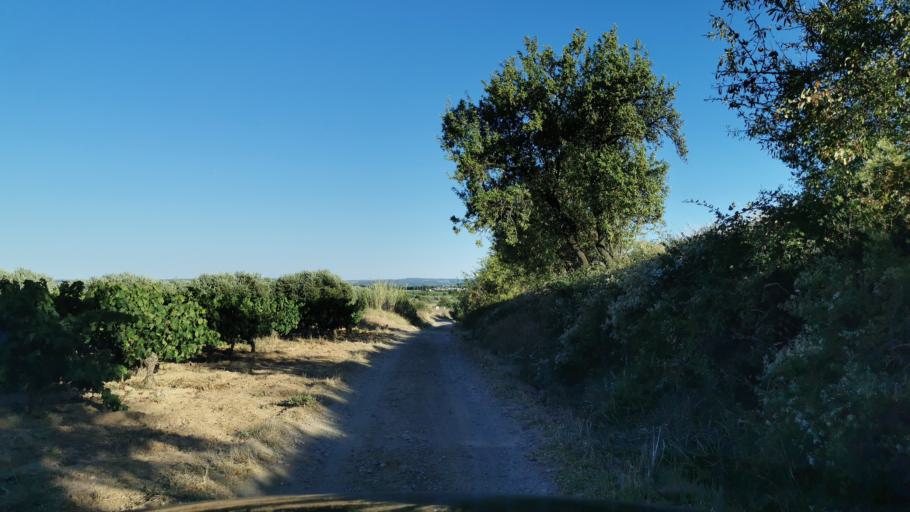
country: FR
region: Languedoc-Roussillon
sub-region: Departement de l'Aude
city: Ouveillan
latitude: 43.2689
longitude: 2.9807
